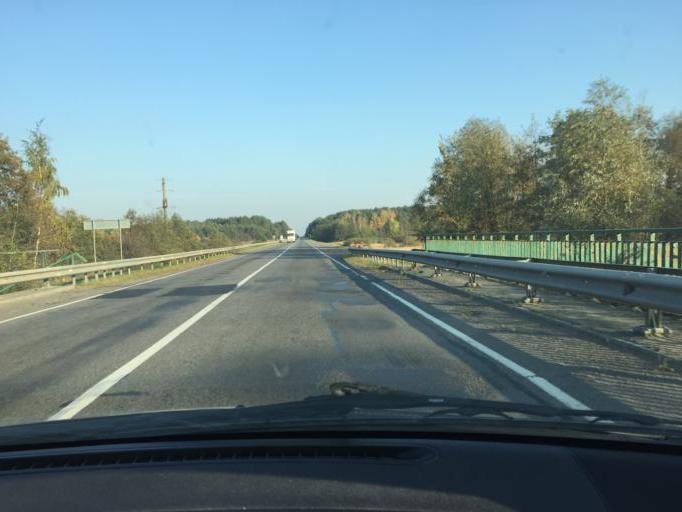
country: BY
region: Brest
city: Davyd-Haradok
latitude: 52.2476
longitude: 27.0877
